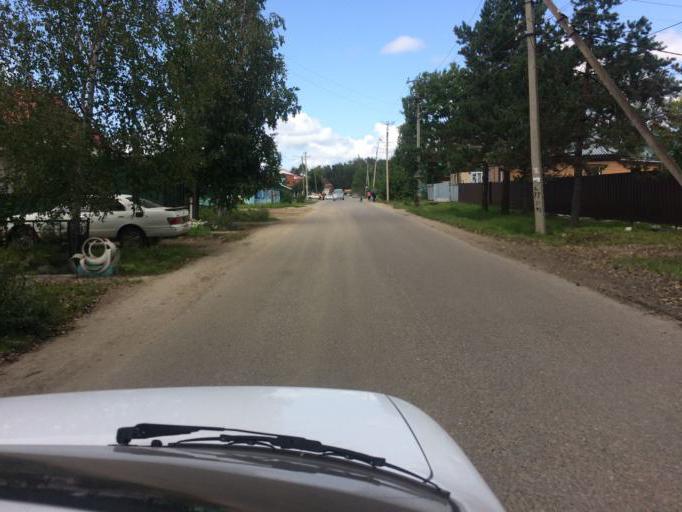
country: RU
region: Primorskiy
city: Dal'nerechensk
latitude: 45.9277
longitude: 133.7313
